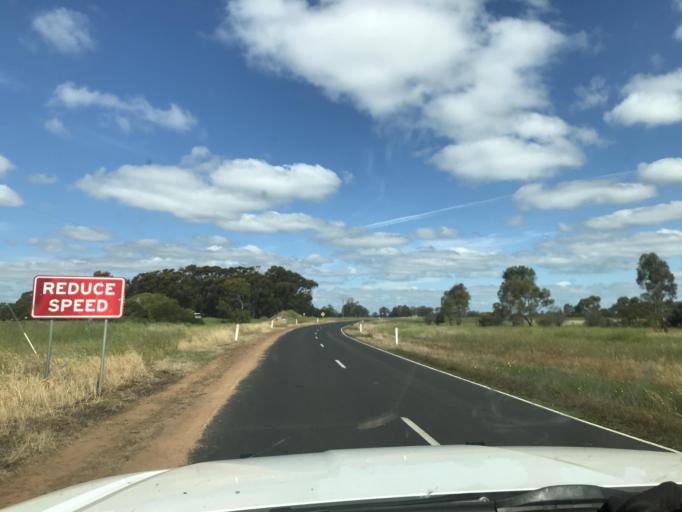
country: AU
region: South Australia
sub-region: Naracoorte and Lucindale
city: Naracoorte
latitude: -37.0194
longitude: 141.3045
